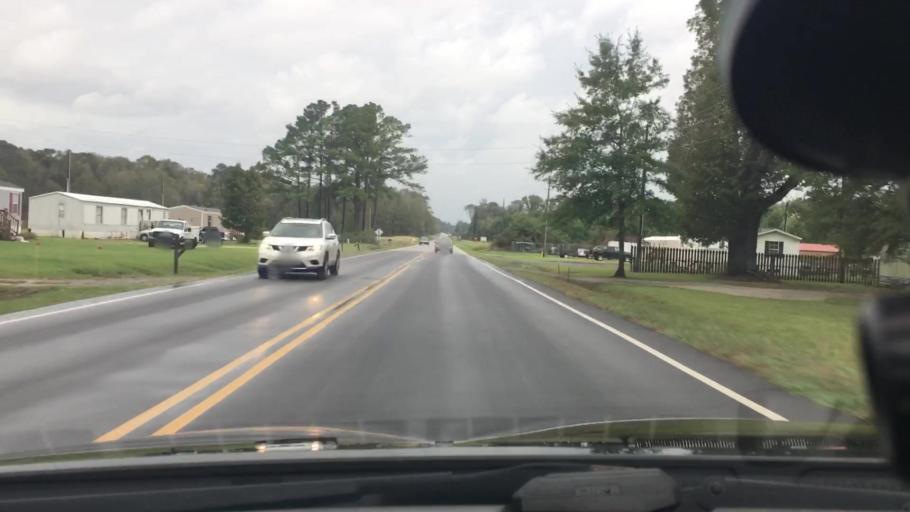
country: US
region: North Carolina
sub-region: Pitt County
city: Windsor
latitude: 35.4534
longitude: -77.2647
